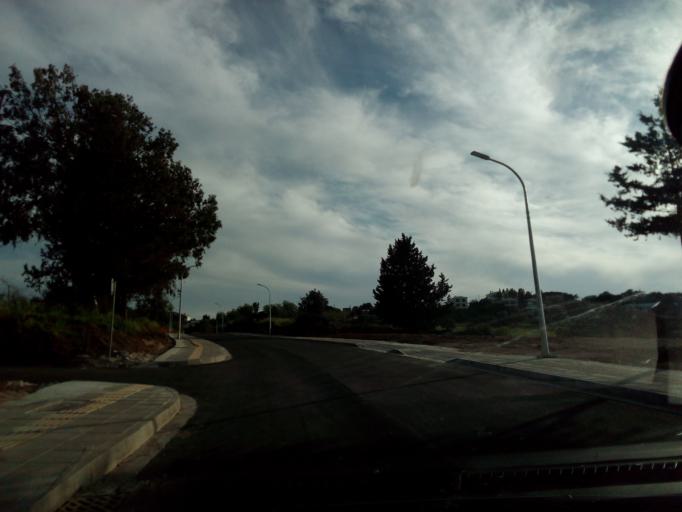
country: CY
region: Pafos
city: Polis
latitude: 35.0279
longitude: 32.3614
